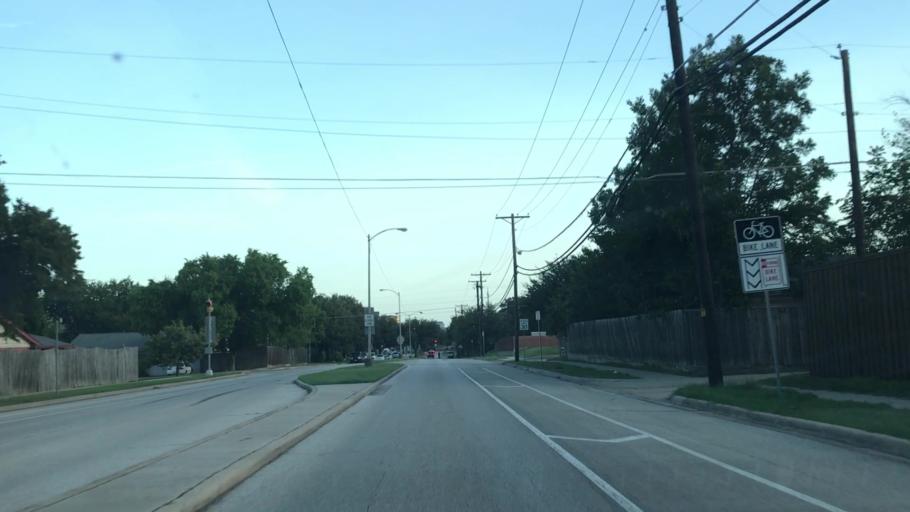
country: US
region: Texas
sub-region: Dallas County
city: Richardson
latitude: 32.9432
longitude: -96.7575
